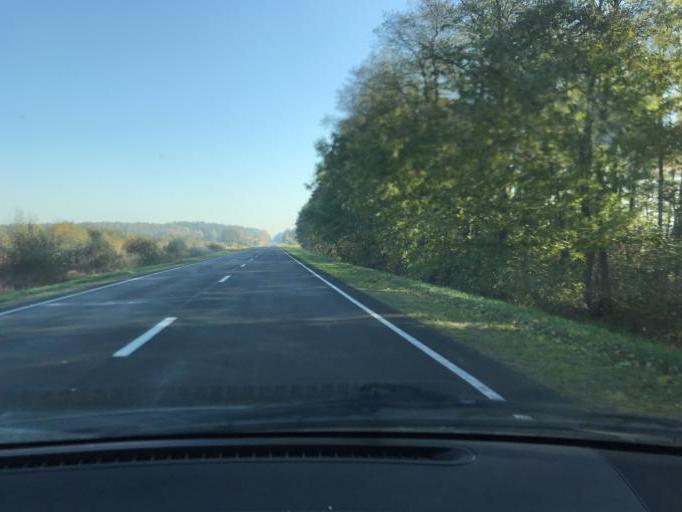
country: BY
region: Brest
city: Baranovichi
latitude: 52.9187
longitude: 25.9698
